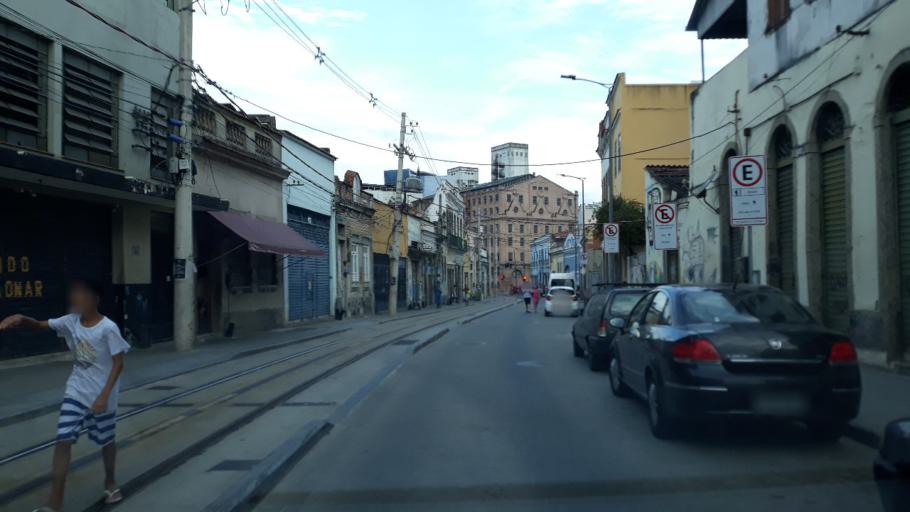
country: BR
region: Rio de Janeiro
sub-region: Rio De Janeiro
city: Rio de Janeiro
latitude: -22.8961
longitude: -43.1933
